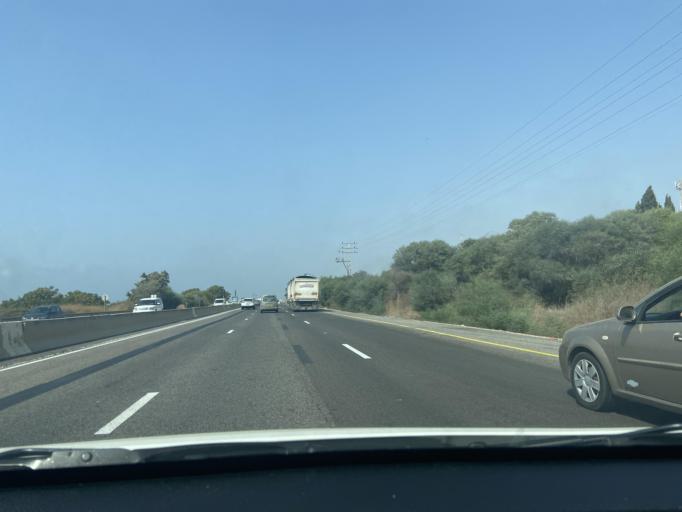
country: IL
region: Northern District
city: El Mazra`a
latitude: 32.9678
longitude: 35.0932
